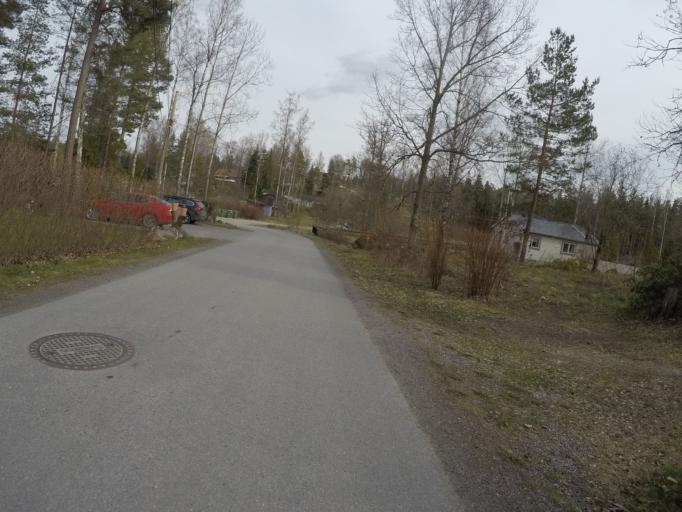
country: SE
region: Soedermanland
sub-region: Eskilstuna Kommun
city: Torshalla
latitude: 59.4462
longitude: 16.5156
